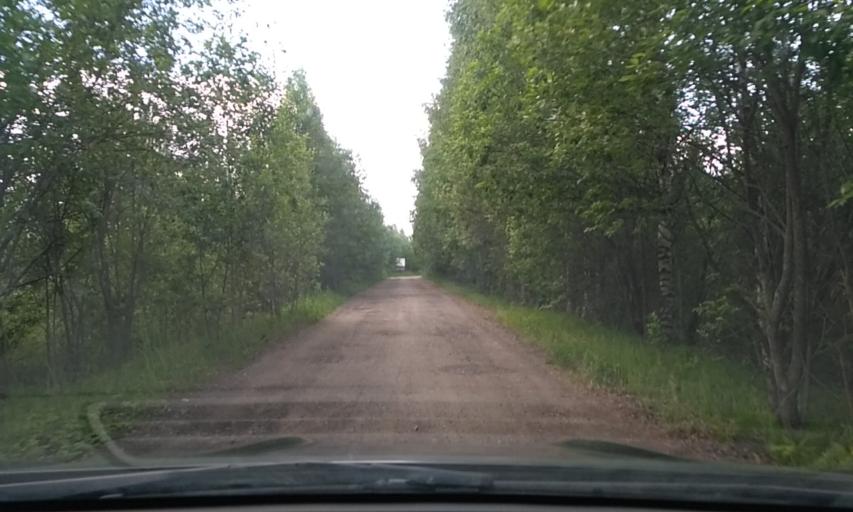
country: RU
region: Leningrad
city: Otradnoye
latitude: 59.8111
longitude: 30.8268
